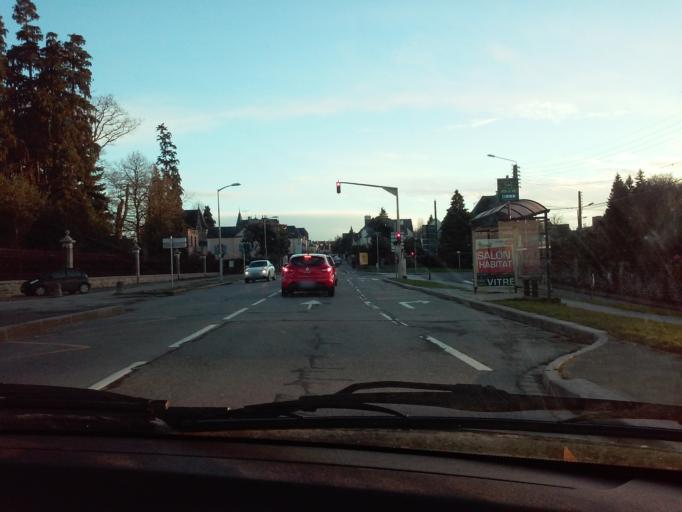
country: FR
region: Brittany
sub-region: Departement d'Ille-et-Vilaine
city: Vitre
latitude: 48.1177
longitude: -1.2102
